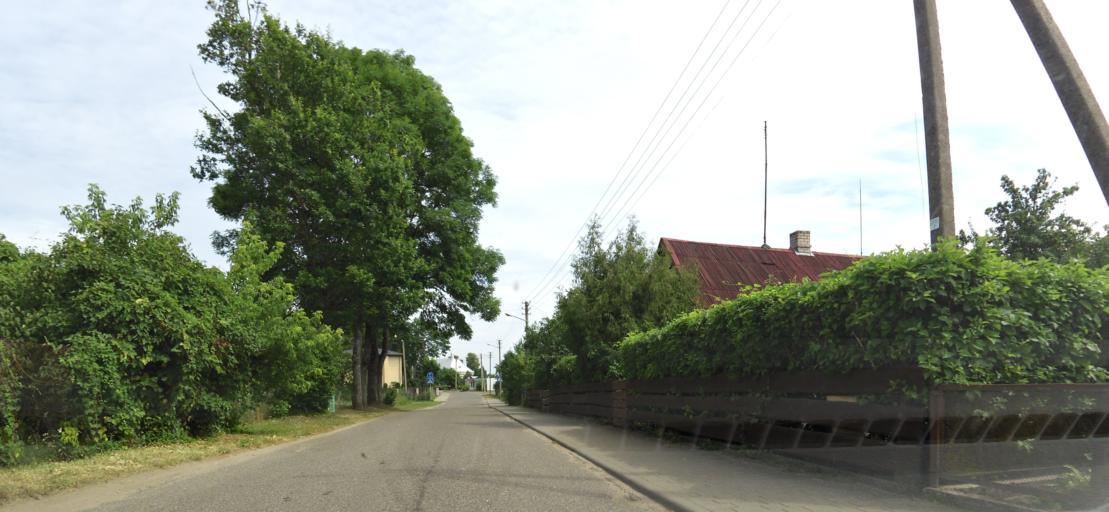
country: LT
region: Vilnius County
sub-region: Trakai
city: Rudiskes
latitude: 54.3562
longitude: 24.8381
